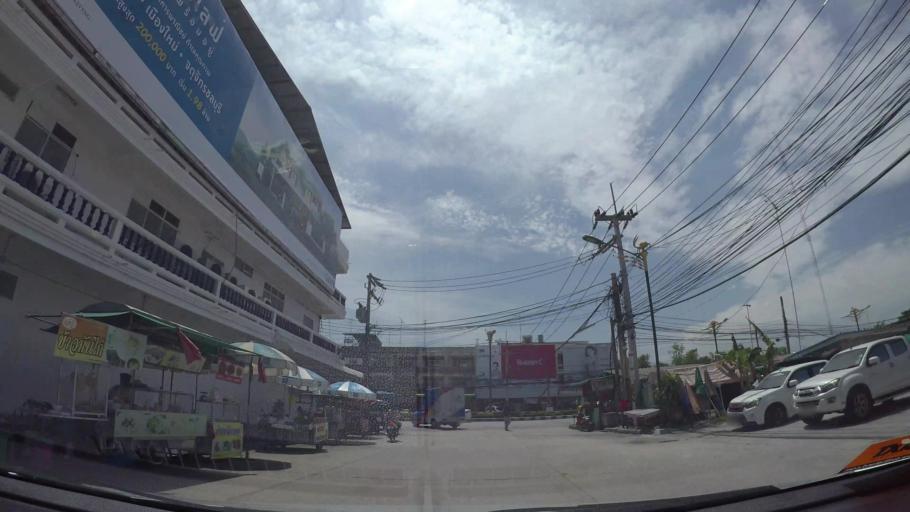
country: TH
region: Chon Buri
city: Chon Buri
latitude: 13.3309
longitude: 100.9517
